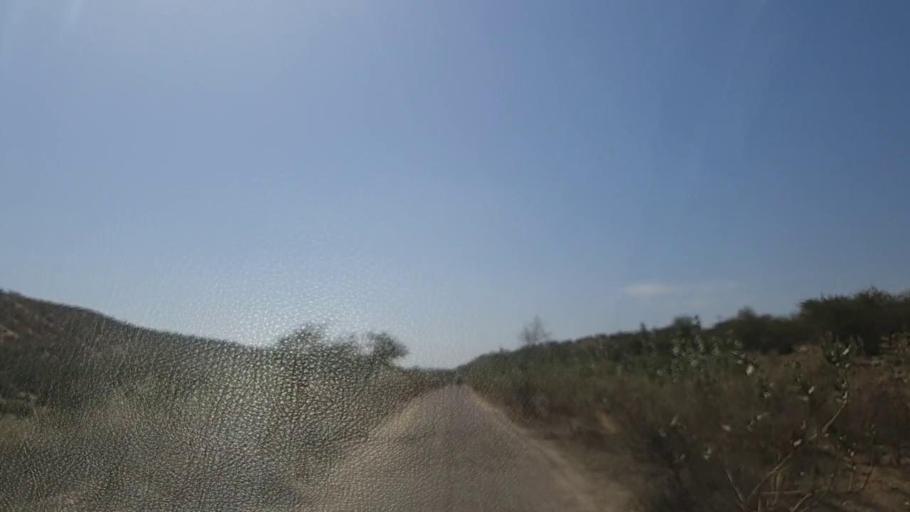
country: PK
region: Sindh
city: Naukot
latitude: 24.8326
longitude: 69.5893
